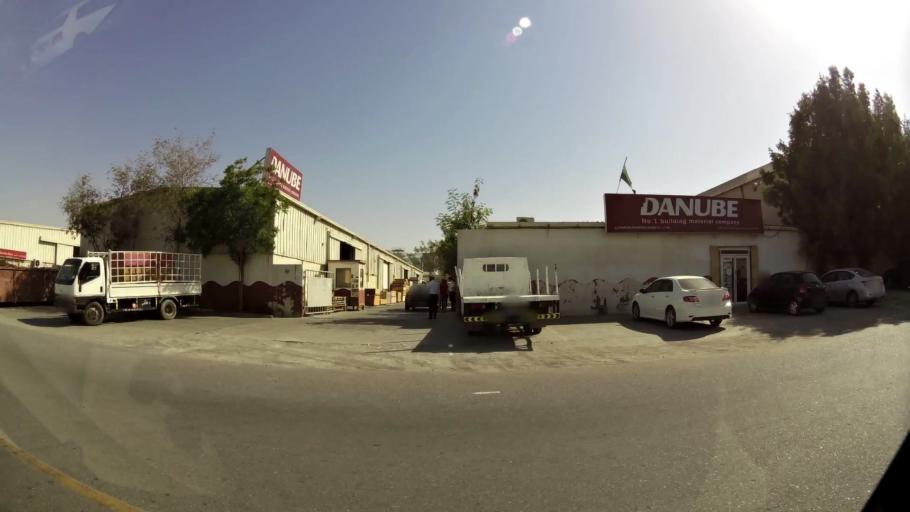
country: AE
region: Dubai
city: Dubai
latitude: 25.1199
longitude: 55.2209
